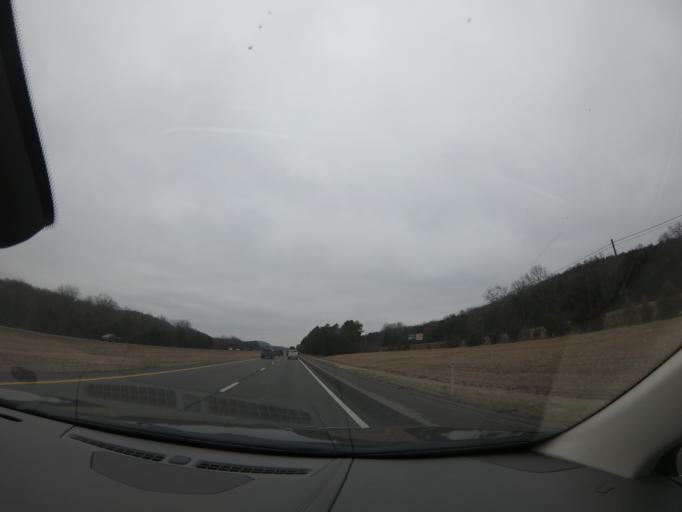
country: US
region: Tennessee
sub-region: Rutherford County
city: Plainview
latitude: 35.6548
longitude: -86.2620
